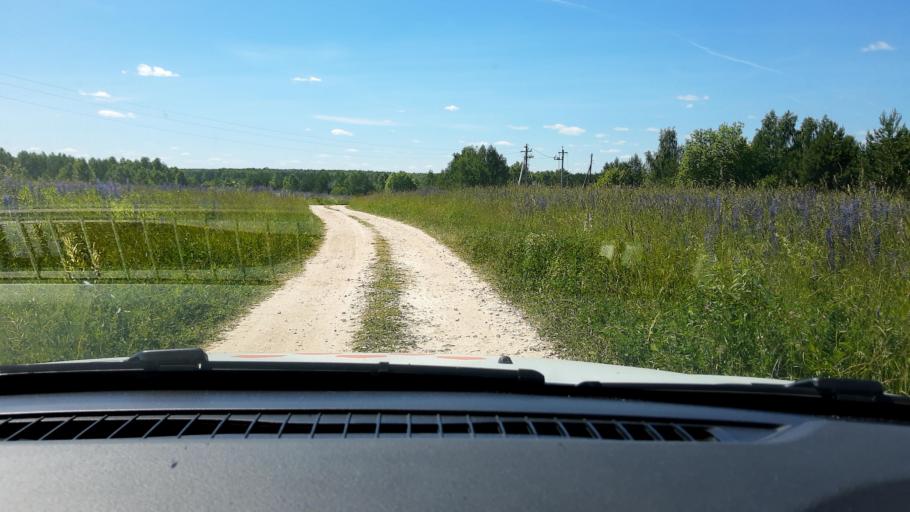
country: RU
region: Nizjnij Novgorod
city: Surovatikha
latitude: 55.8697
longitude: 43.9704
